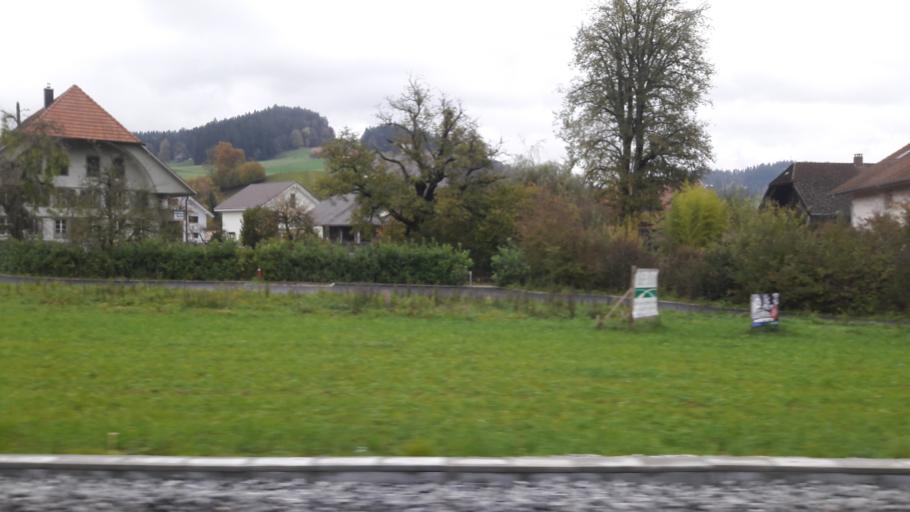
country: CH
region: Bern
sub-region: Emmental District
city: Trachselwald
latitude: 47.0081
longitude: 7.7241
